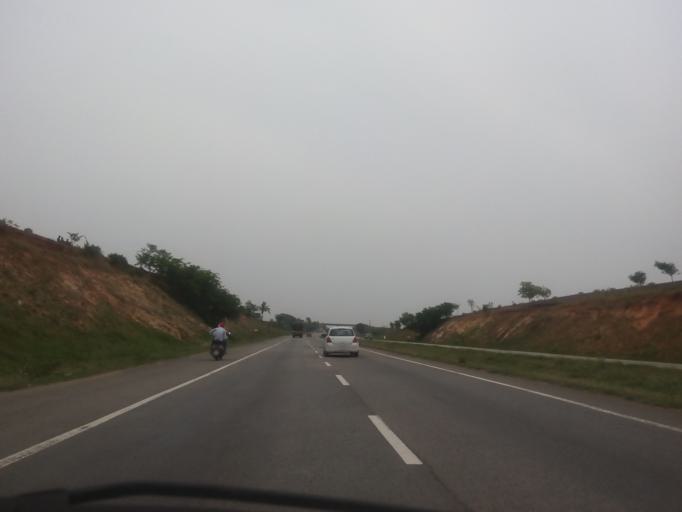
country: IN
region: Karnataka
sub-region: Bangalore Urban
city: Bangalore
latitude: 12.9774
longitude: 77.4712
